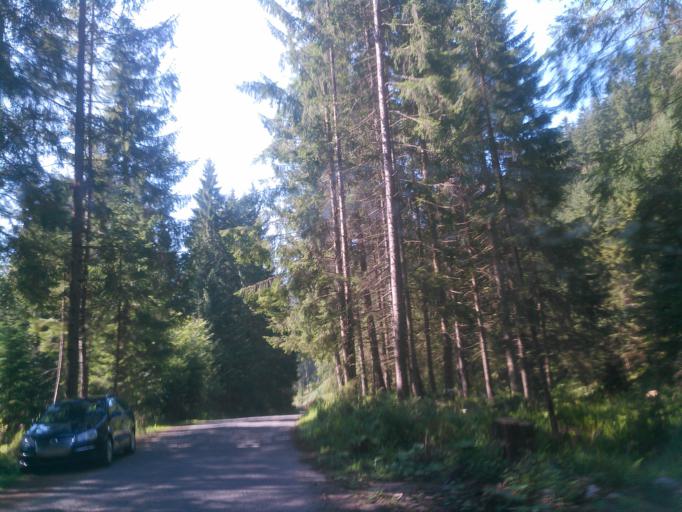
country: SK
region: Zilinsky
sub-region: Okres Liptovsky Mikulas
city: Liptovsky Mikulas
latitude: 48.9955
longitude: 19.5045
